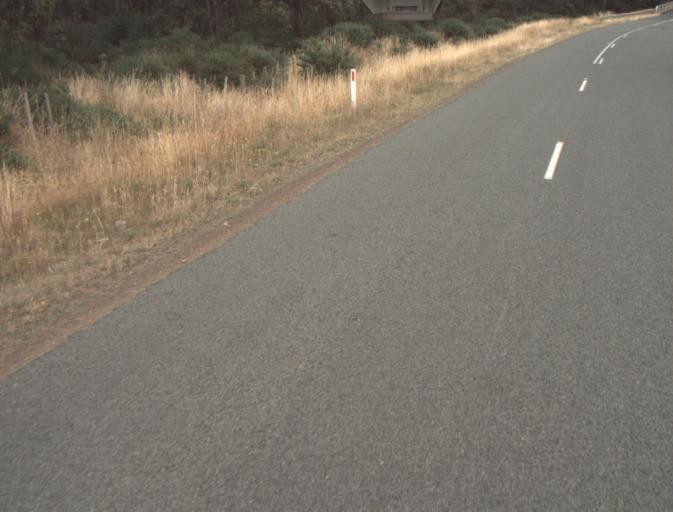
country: AU
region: Tasmania
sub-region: Northern Midlands
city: Evandale
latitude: -41.4882
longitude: 147.5026
